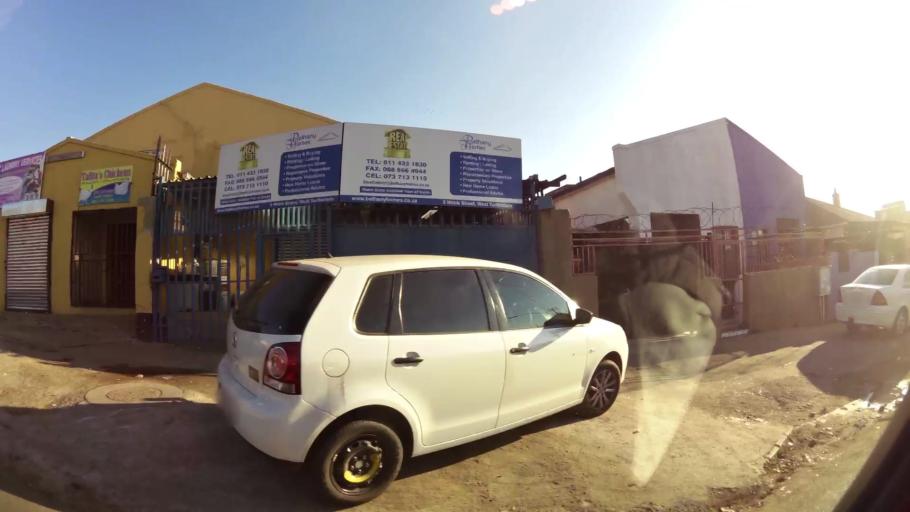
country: ZA
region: Gauteng
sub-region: City of Johannesburg Metropolitan Municipality
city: Johannesburg
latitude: -26.2391
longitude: 28.0262
